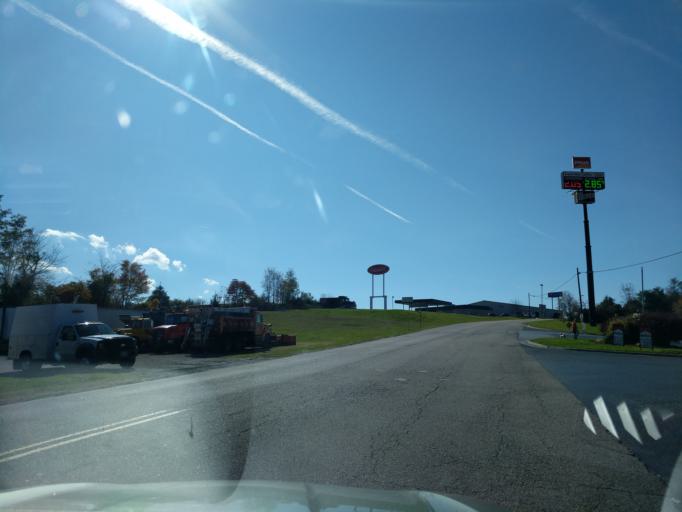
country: US
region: Virginia
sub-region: Augusta County
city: Stuarts Draft
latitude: 37.9321
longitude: -79.2309
